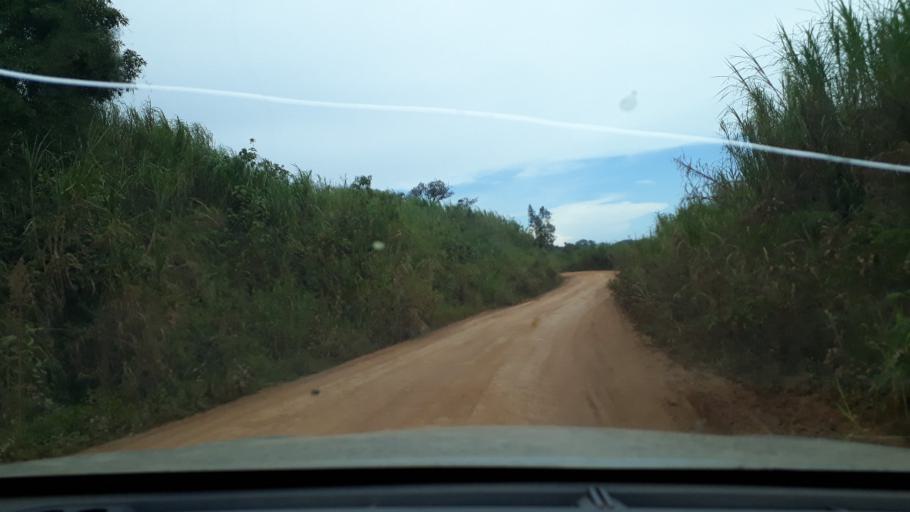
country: CD
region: Eastern Province
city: Bunia
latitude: 1.8253
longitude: 30.4467
